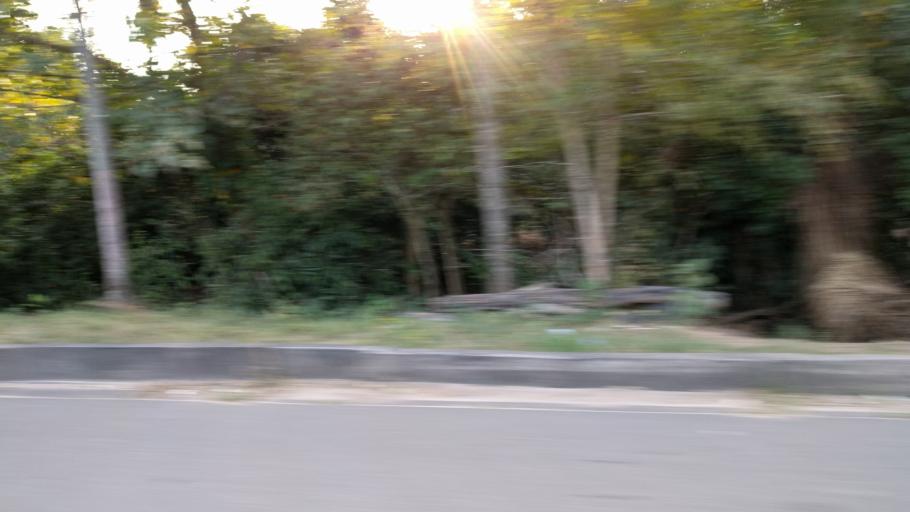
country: BO
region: Santa Cruz
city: Buena Vista
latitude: -17.4135
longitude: -63.6162
